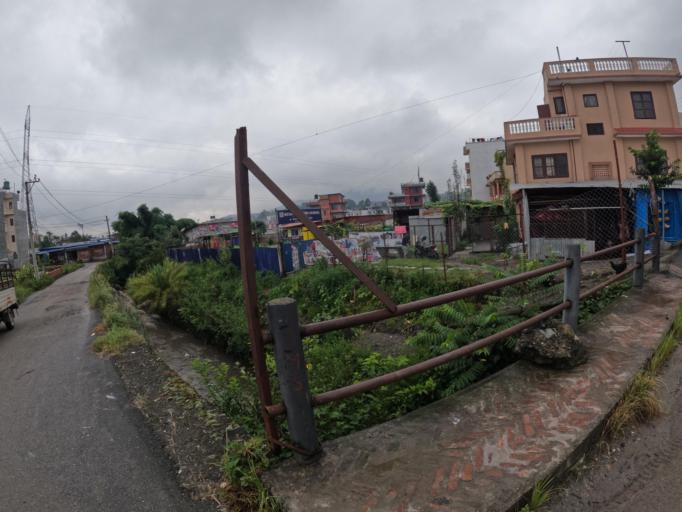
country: NP
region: Central Region
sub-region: Bagmati Zone
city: Kathmandu
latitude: 27.7642
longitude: 85.3195
